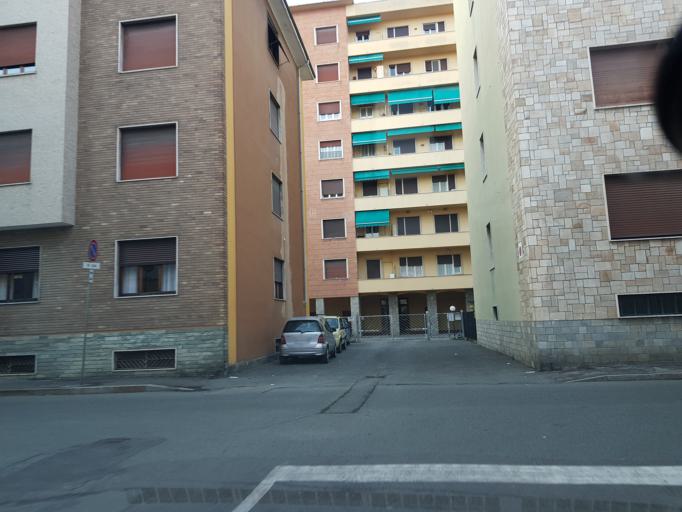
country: IT
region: Piedmont
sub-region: Provincia di Alessandria
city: Novi Ligure
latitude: 44.7632
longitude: 8.7905
